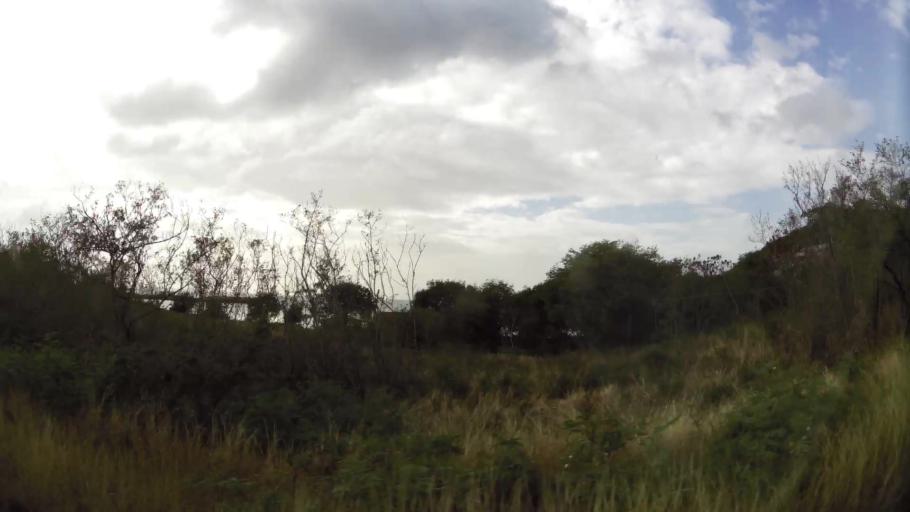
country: KN
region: Saint Thomas Lowland
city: Cotton Ground
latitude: 17.1900
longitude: -62.6166
